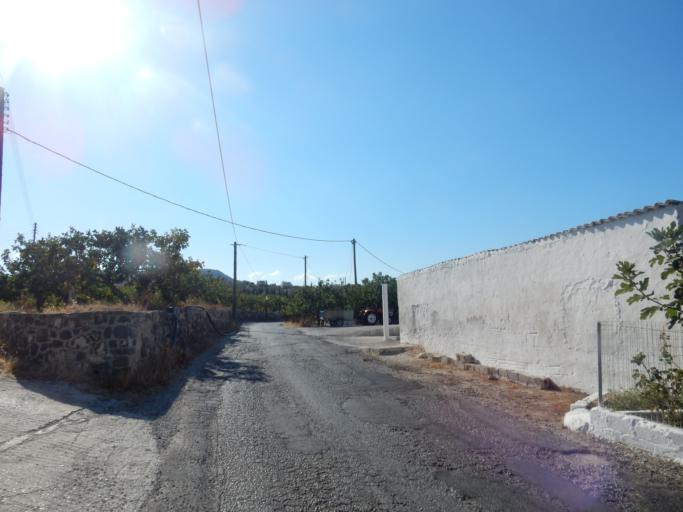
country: GR
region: Attica
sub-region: Nomos Piraios
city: Kypseli
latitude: 37.7354
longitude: 23.4521
